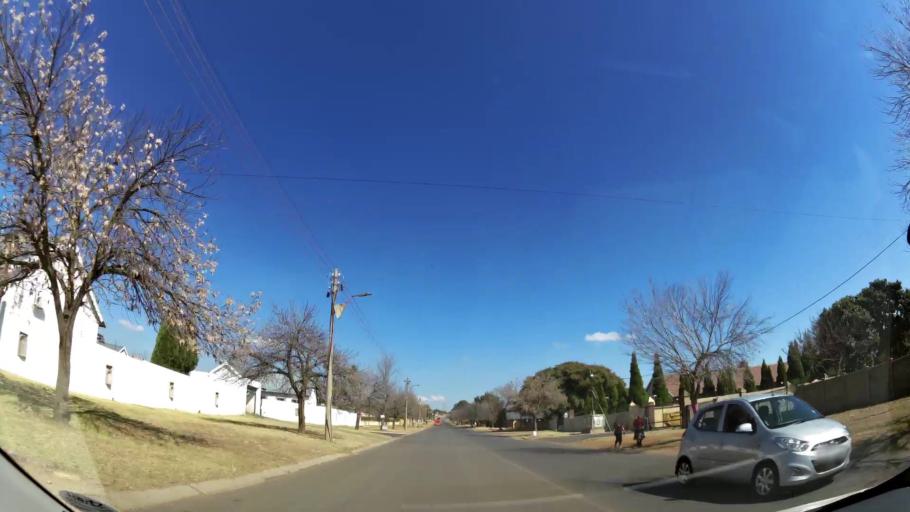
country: ZA
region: Mpumalanga
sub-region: Nkangala District Municipality
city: Witbank
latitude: -25.8508
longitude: 29.2492
